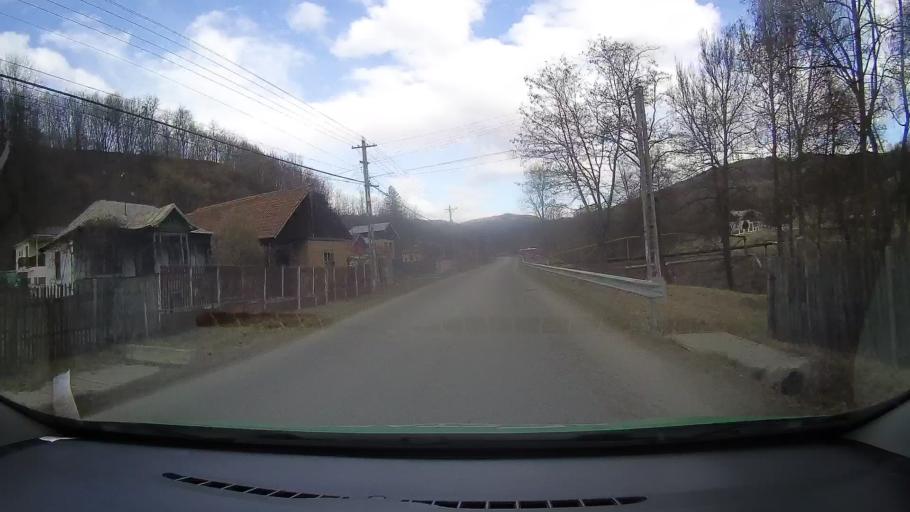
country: RO
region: Dambovita
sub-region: Comuna Visinesti
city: Visinesti
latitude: 45.0689
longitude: 25.5464
